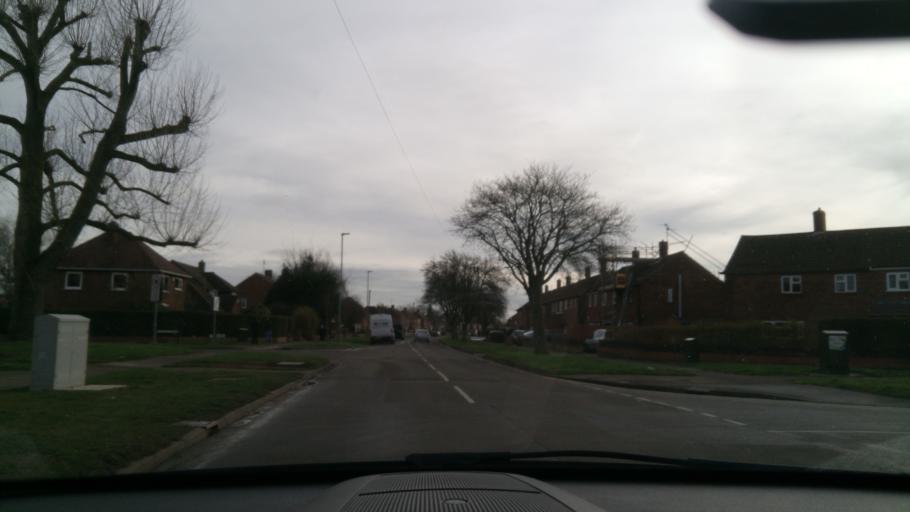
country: GB
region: England
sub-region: Peterborough
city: Peterborough
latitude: 52.5985
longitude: -0.2259
